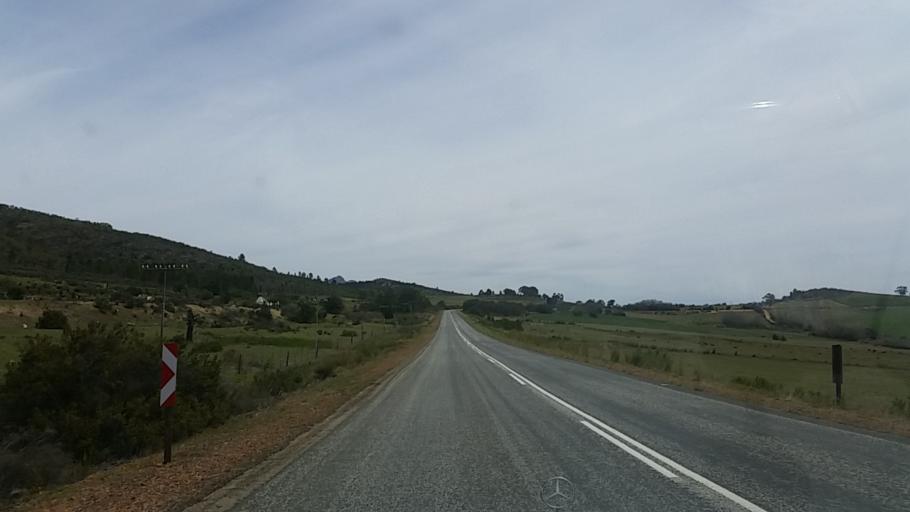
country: ZA
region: Western Cape
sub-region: Eden District Municipality
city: Knysna
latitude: -33.7733
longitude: 22.9164
